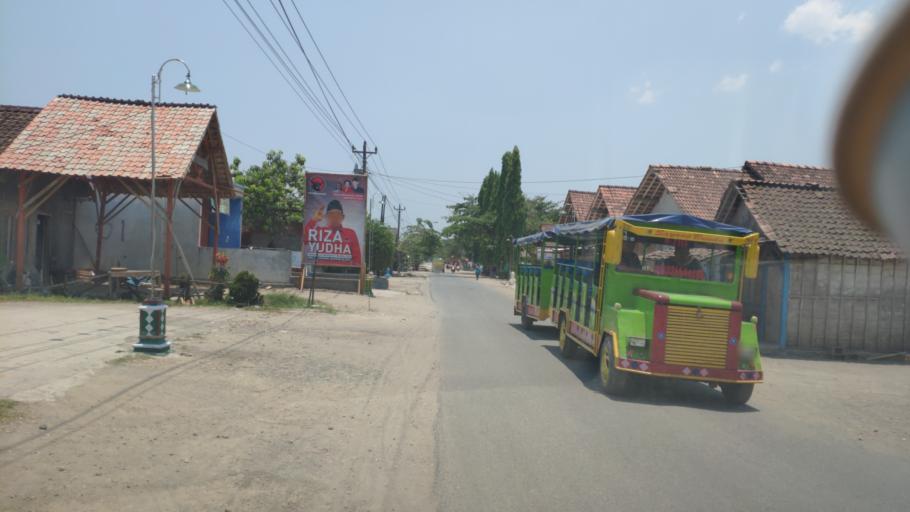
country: ID
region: Central Java
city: Mendenrejo
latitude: -7.2371
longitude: 111.4406
